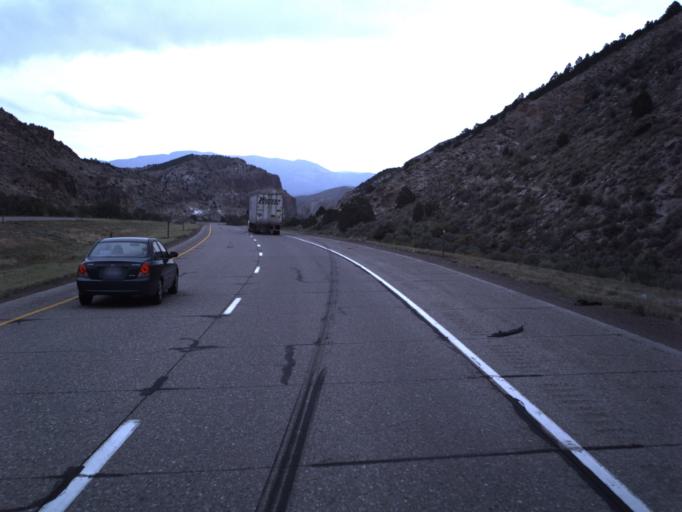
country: US
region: Utah
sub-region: Sevier County
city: Monroe
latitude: 38.5774
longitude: -112.3201
